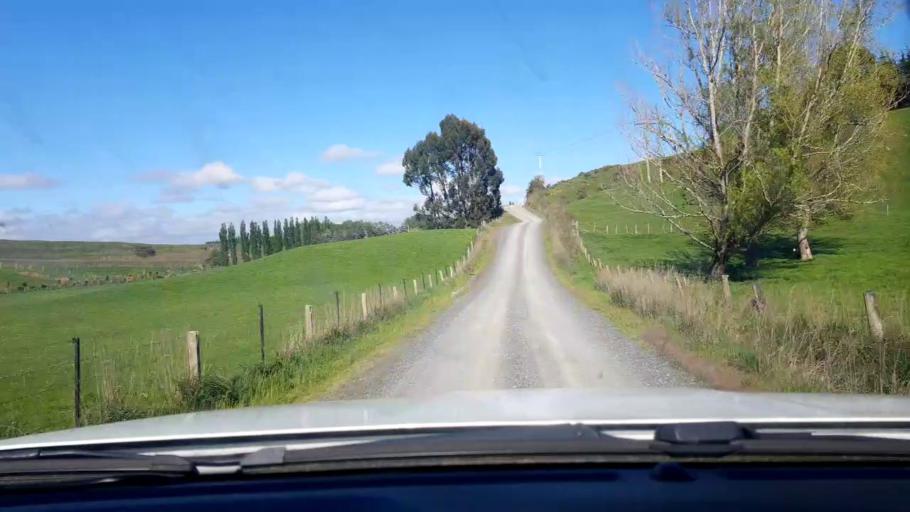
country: NZ
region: Otago
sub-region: Clutha District
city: Balclutha
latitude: -46.2234
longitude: 169.7392
